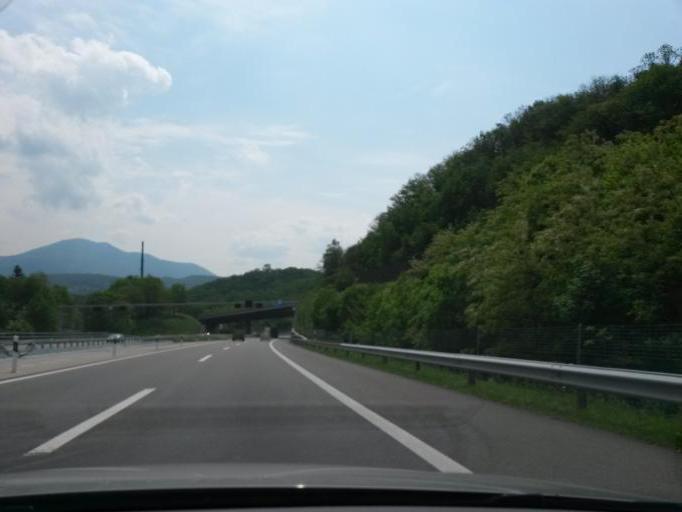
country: CH
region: Ticino
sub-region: Lugano District
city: Gravesano
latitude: 46.0748
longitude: 8.9261
